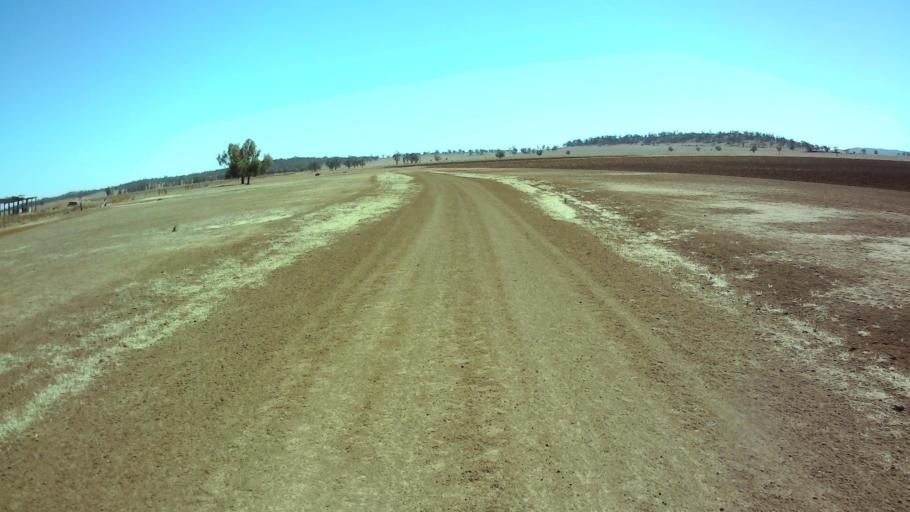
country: AU
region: New South Wales
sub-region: Forbes
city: Forbes
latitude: -33.7069
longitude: 147.6683
